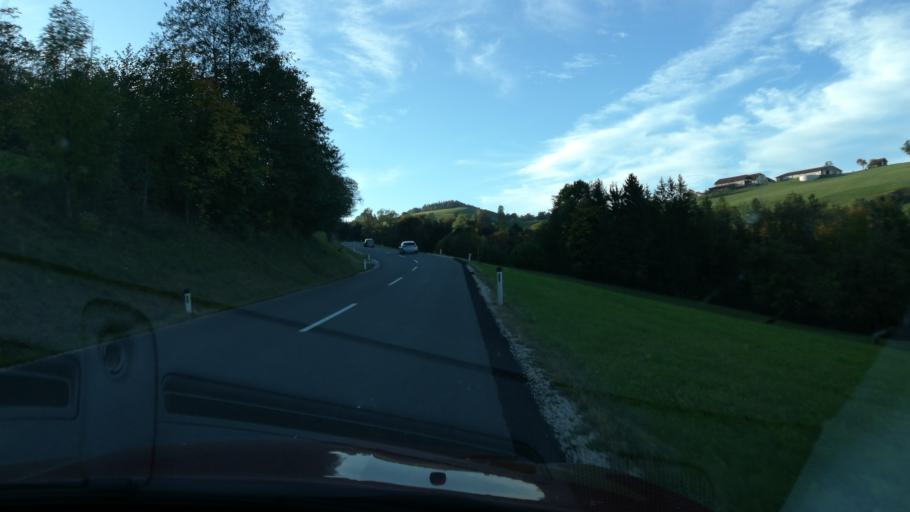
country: AT
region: Upper Austria
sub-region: Politischer Bezirk Kirchdorf an der Krems
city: Gruenburg
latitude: 47.9623
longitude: 14.3112
